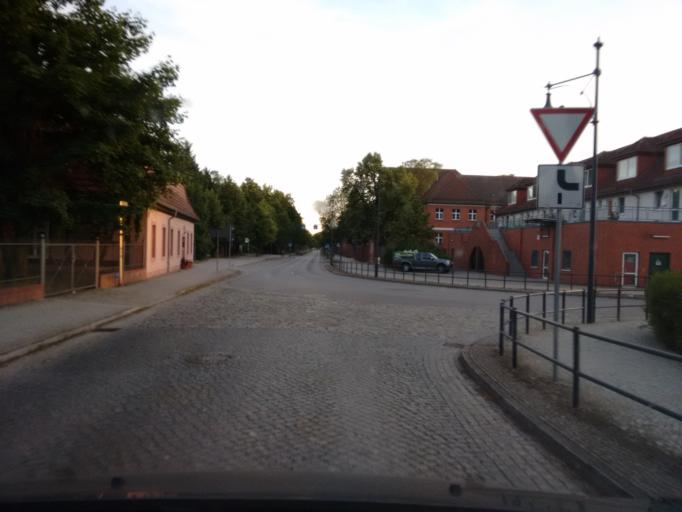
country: DE
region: Brandenburg
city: Beeskow
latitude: 52.1700
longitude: 14.2451
